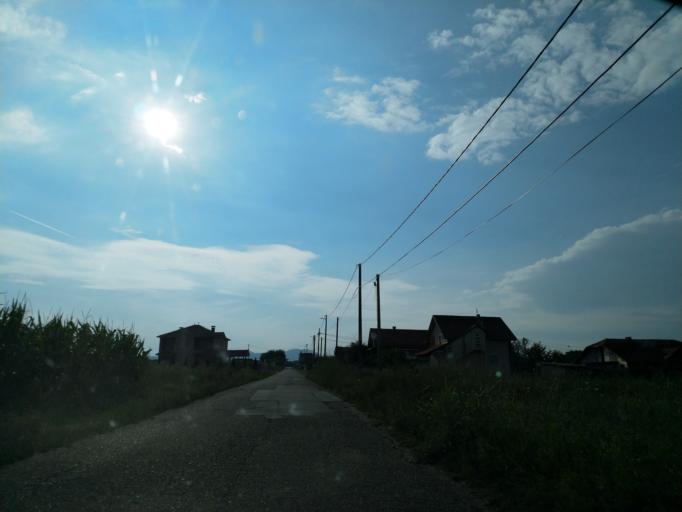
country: RS
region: Central Serbia
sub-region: Pomoravski Okrug
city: Jagodina
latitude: 43.9778
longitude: 21.2355
